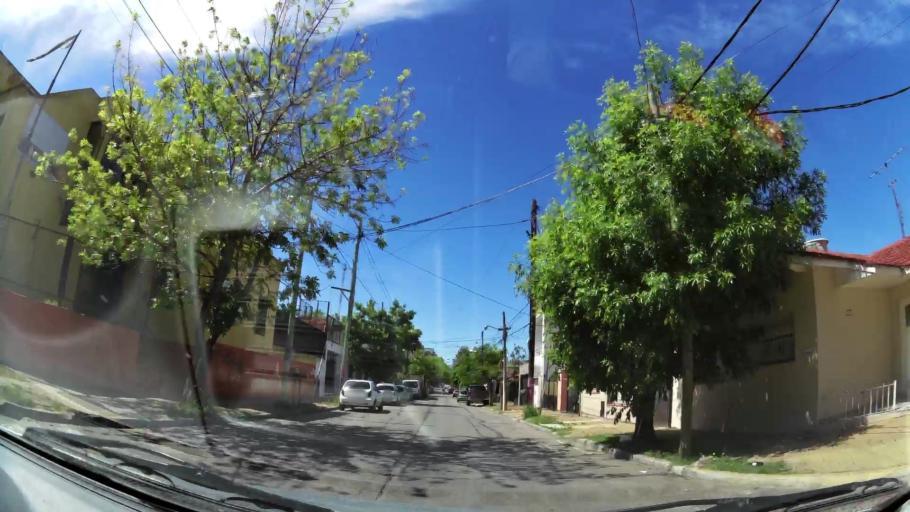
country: AR
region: Buenos Aires
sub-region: Partido de Quilmes
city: Quilmes
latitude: -34.7128
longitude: -58.2629
